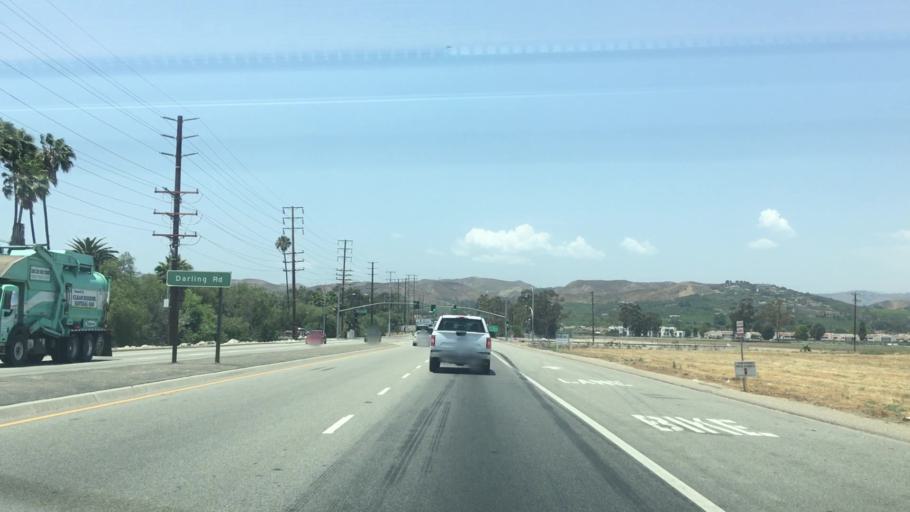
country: US
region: California
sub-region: Ventura County
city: Saticoy
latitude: 34.2854
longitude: -119.1526
